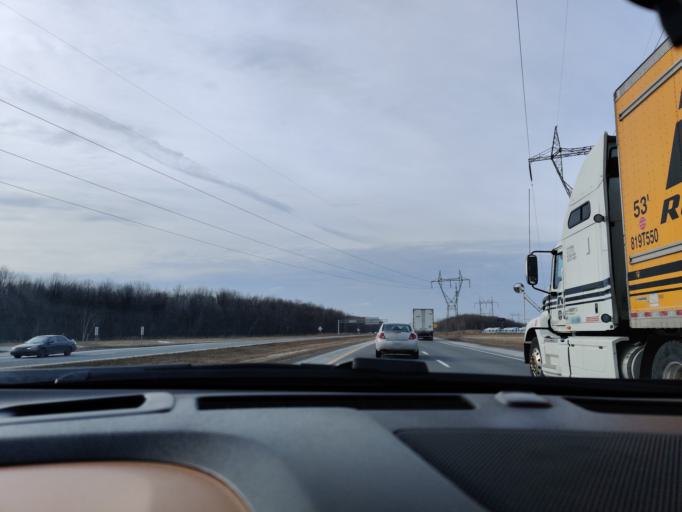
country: CA
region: Quebec
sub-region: Monteregie
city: Les Coteaux
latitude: 45.2664
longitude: -74.2230
